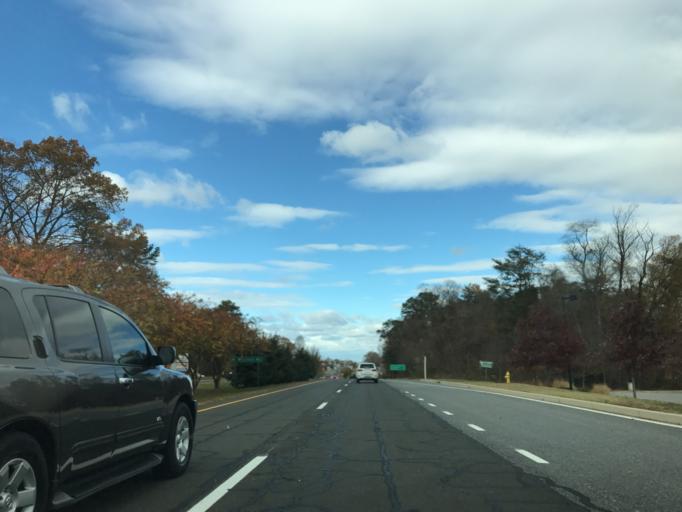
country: US
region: Maryland
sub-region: Anne Arundel County
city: Pasadena
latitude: 39.1168
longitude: -76.5812
